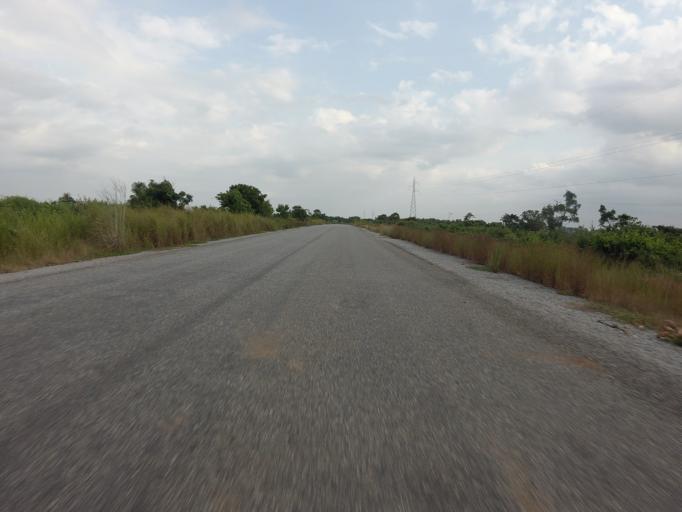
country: GH
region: Volta
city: Ho
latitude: 6.4013
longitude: 0.5249
